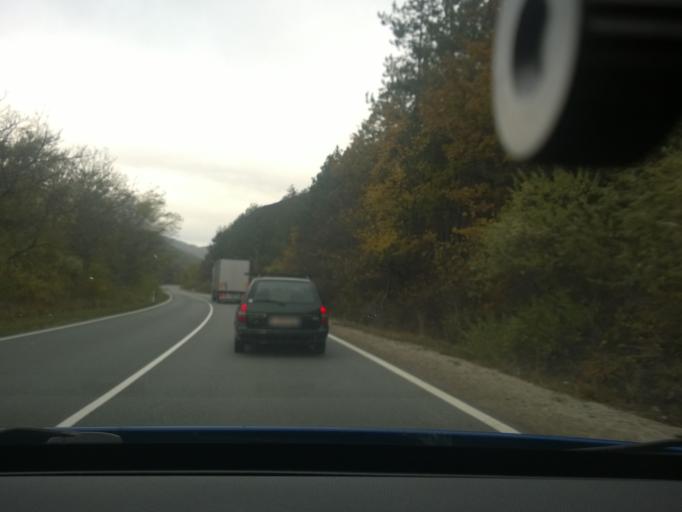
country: BG
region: Sofiya
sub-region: Obshtina Dragoman
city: Dragoman
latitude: 42.9624
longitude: 22.8921
